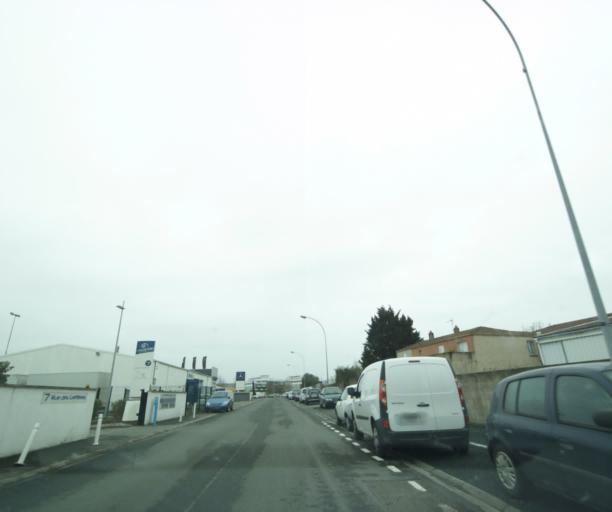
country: FR
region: Poitou-Charentes
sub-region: Departement de la Charente-Maritime
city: Lagord
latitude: 46.1881
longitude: -1.1476
